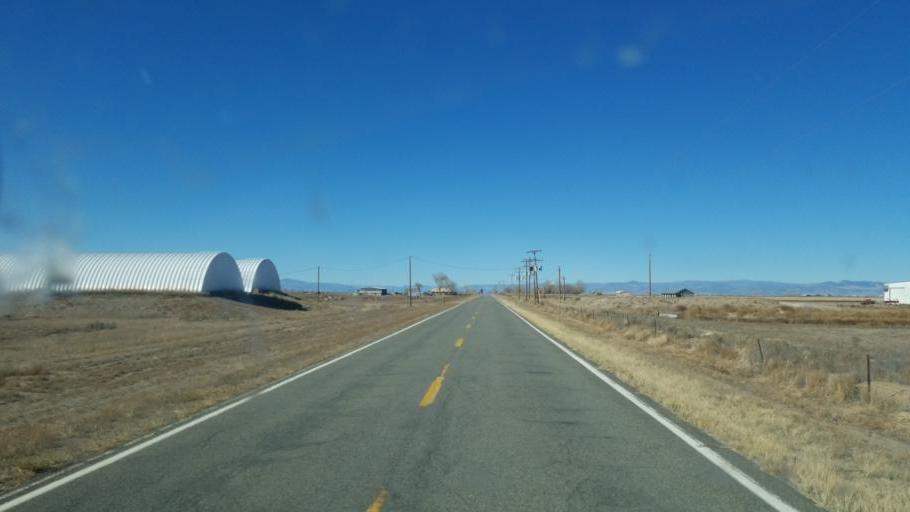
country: US
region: Colorado
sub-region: Saguache County
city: Center
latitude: 37.7493
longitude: -105.8991
